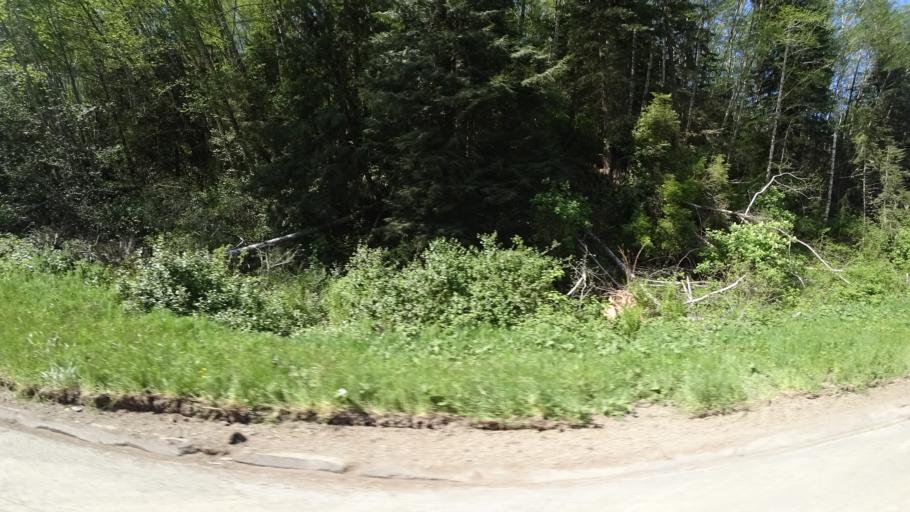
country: US
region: California
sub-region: Del Norte County
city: Bertsch-Oceanview
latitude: 41.4590
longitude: -124.0322
